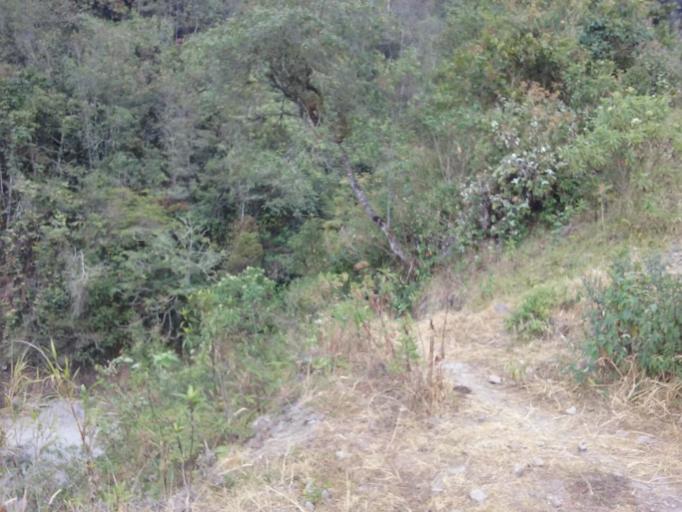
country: CO
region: Tolima
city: Cajamarca
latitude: 4.4746
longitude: -75.3883
